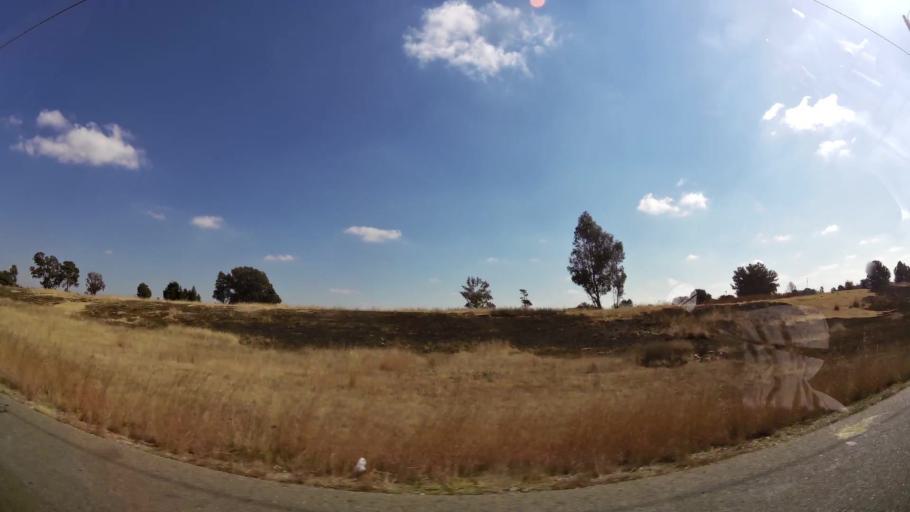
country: ZA
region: Gauteng
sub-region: West Rand District Municipality
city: Randfontein
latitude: -26.1575
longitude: 27.7622
